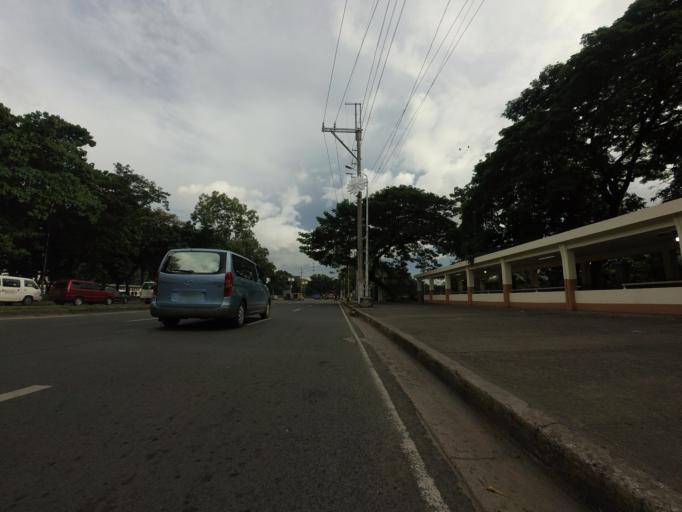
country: PH
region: Metro Manila
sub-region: City of Manila
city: Quiapo
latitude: 14.5931
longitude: 120.9791
